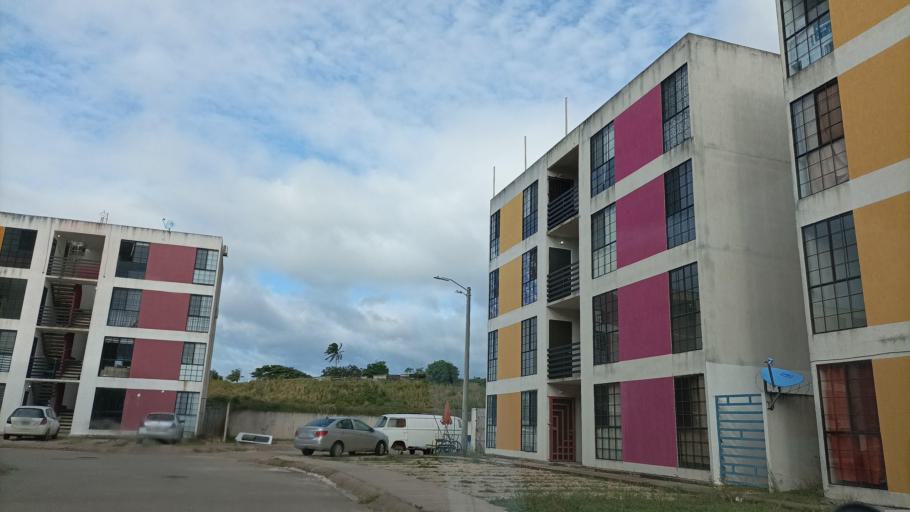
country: MX
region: Veracruz
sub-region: Coatzacoalcos
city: Fraccionamiento Ciudad Olmeca
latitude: 18.1569
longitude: -94.5593
